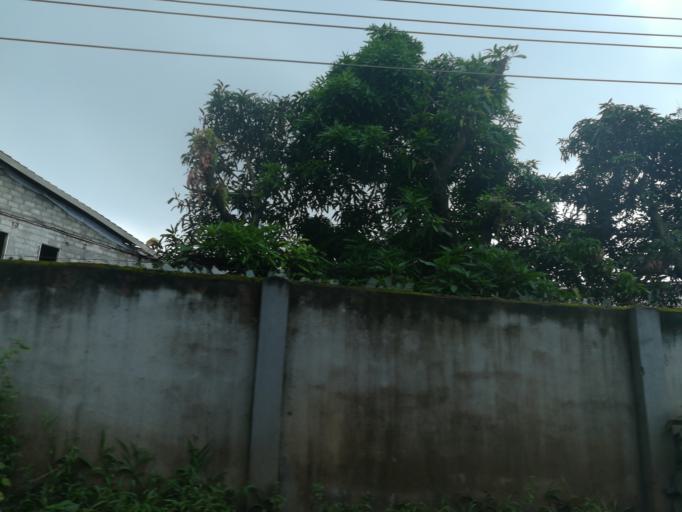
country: NG
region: Lagos
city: Ojota
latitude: 6.5682
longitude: 3.3680
